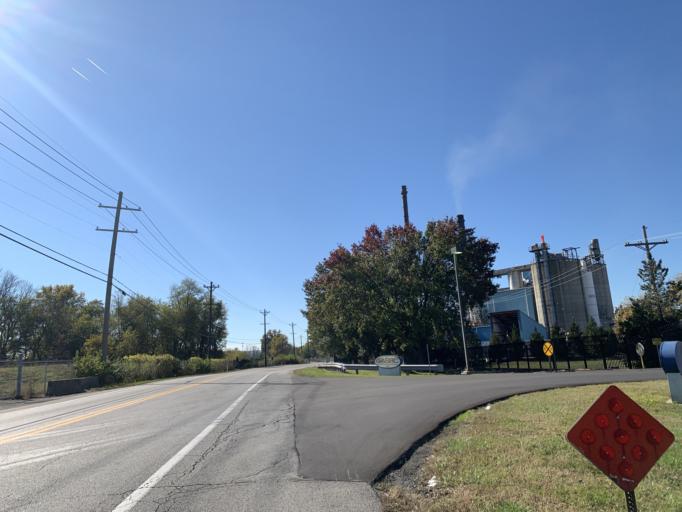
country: US
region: Kentucky
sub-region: Jefferson County
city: Saint Dennis
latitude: 38.2083
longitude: -85.8449
